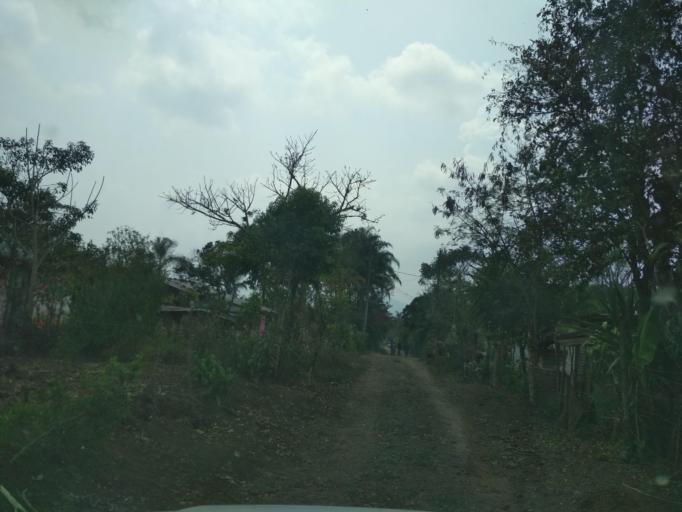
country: MX
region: Veracruz
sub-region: Cordoba
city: Fredepo
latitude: 18.8565
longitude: -96.9795
